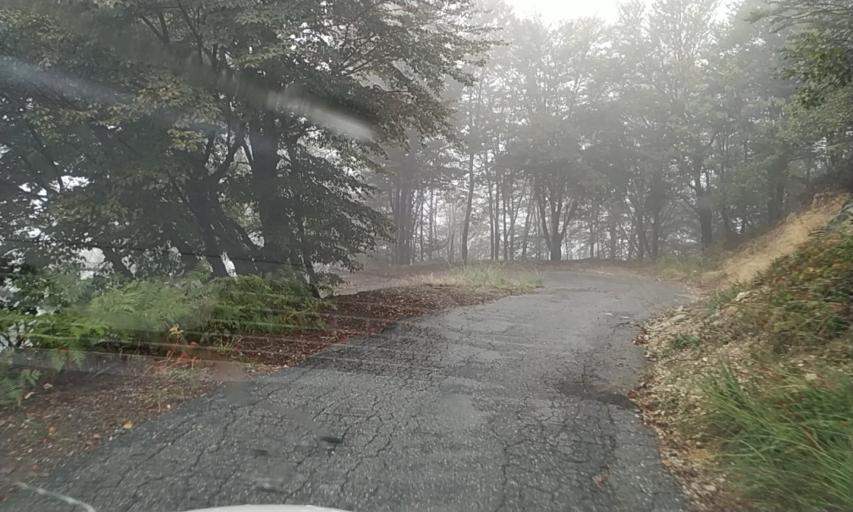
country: IT
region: Piedmont
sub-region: Provincia di Vercelli
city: Civiasco
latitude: 45.8304
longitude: 8.2990
